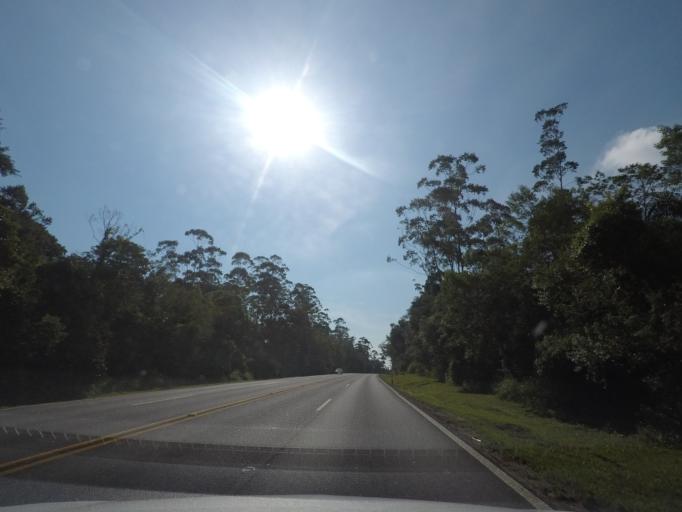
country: BR
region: Parana
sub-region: Paranagua
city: Paranagua
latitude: -25.6026
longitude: -48.6090
